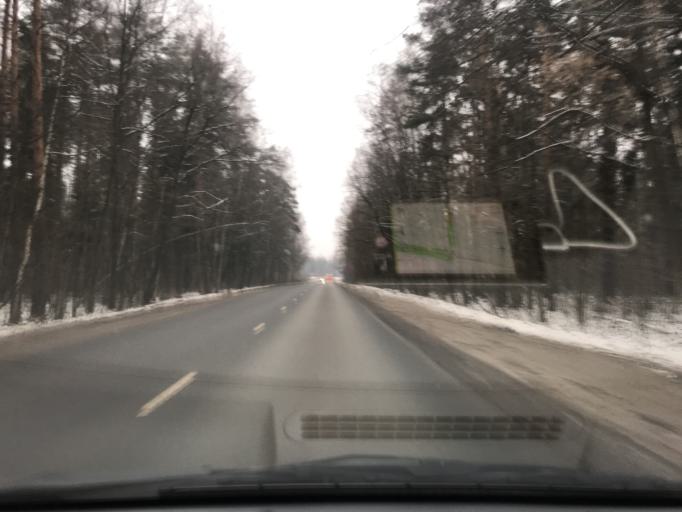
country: RU
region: Moskovskaya
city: Elektrostal'
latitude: 55.8274
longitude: 38.4517
